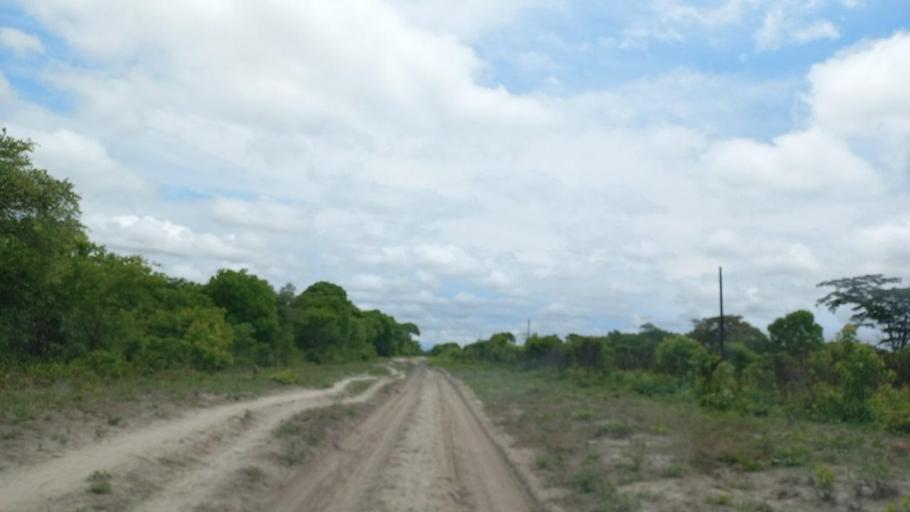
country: ZM
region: North-Western
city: Kabompo
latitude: -13.1836
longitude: 23.9519
